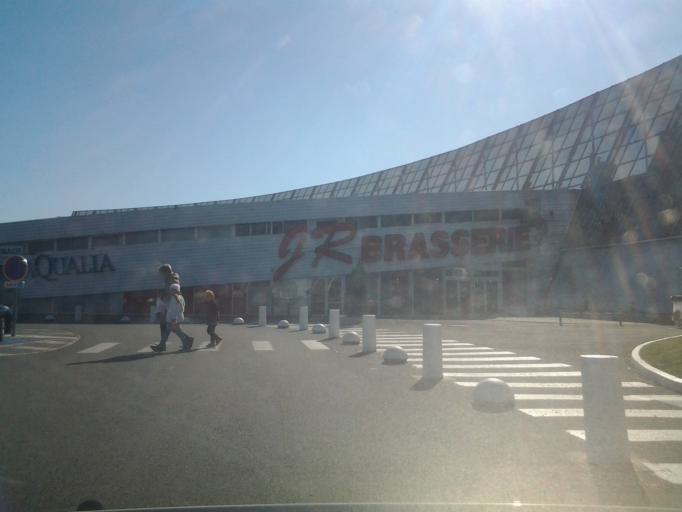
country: FR
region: Pays de la Loire
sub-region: Departement de la Vendee
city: La Roche-sur-Yon
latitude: 46.6974
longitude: -1.4326
